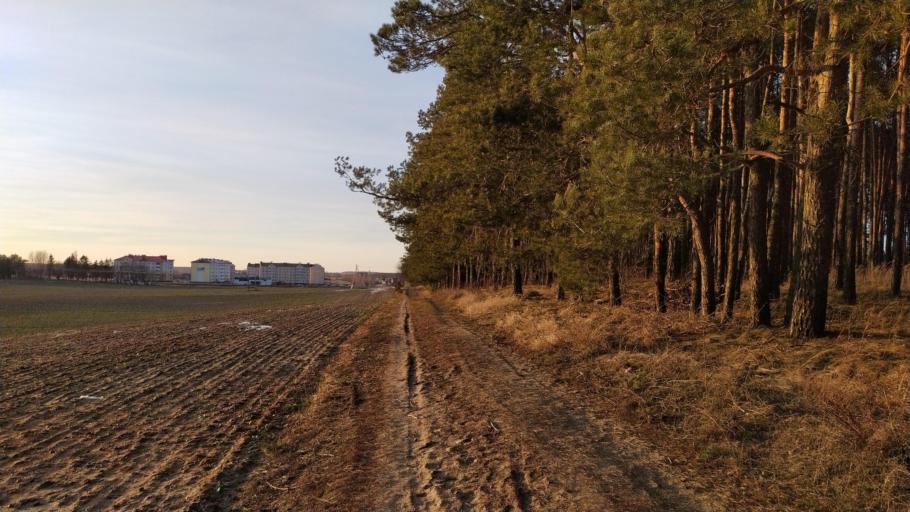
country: BY
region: Brest
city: Kamyanyets
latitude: 52.3867
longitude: 23.8256
